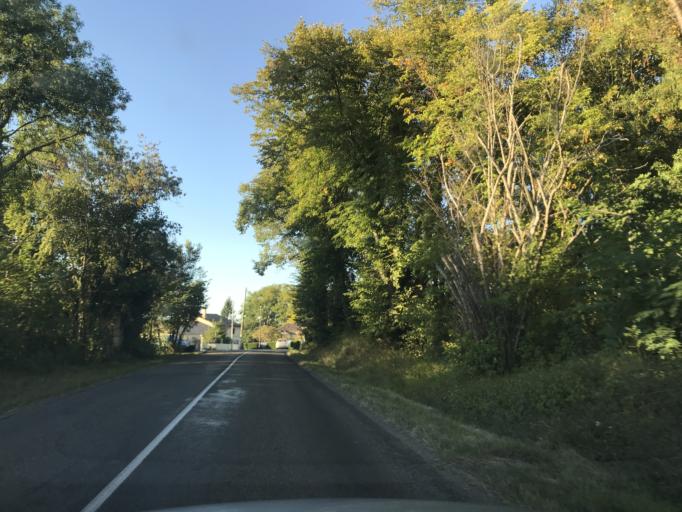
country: FR
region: Aquitaine
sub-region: Departement de la Gironde
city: Lussac
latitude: 44.9432
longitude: -0.0719
